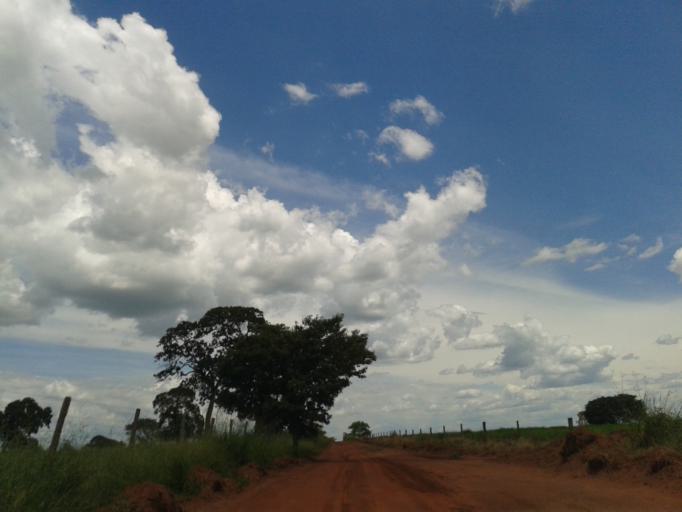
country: BR
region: Minas Gerais
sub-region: Ituiutaba
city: Ituiutaba
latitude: -18.8769
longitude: -49.4792
